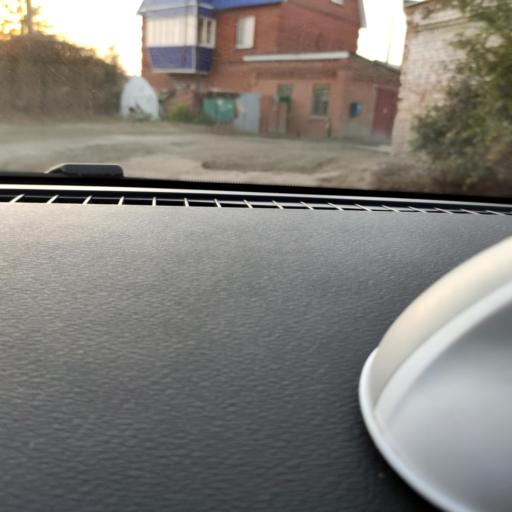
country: RU
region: Samara
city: Samara
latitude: 53.1727
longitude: 50.1694
